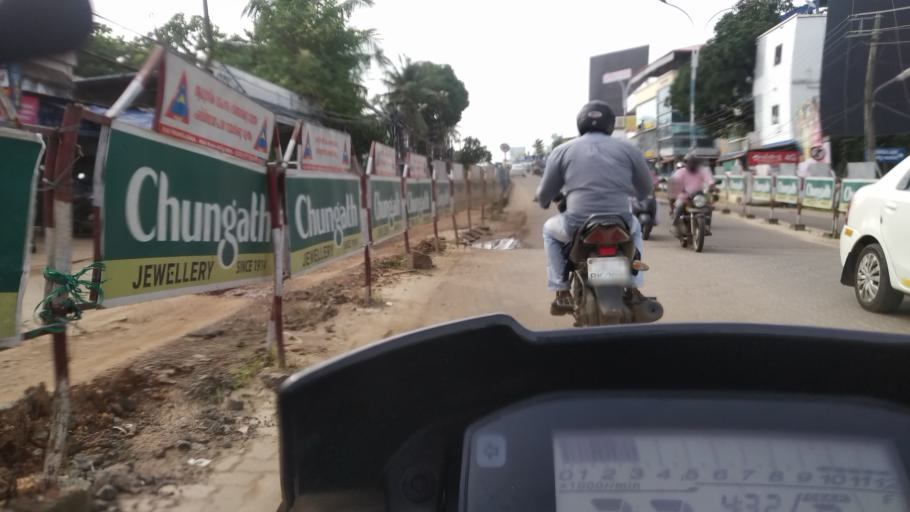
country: IN
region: Kerala
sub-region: Ernakulam
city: Cochin
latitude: 9.9732
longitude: 76.3164
